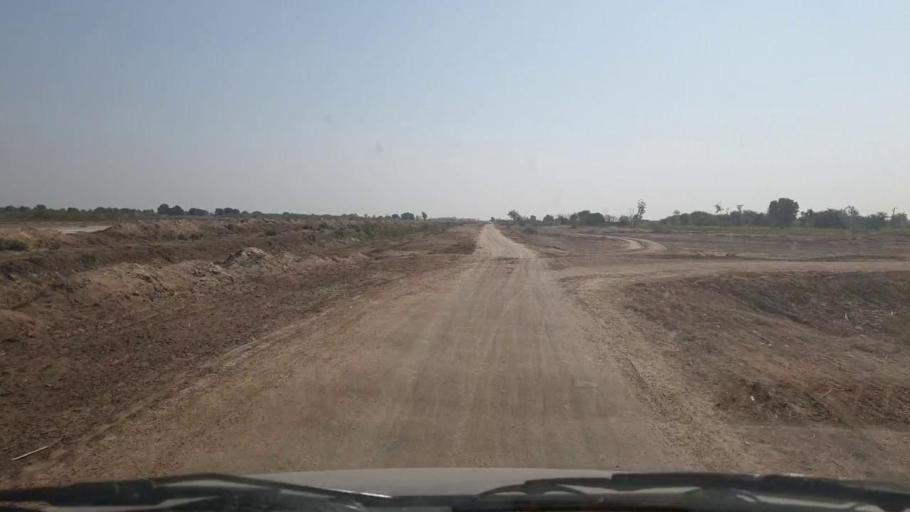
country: PK
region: Sindh
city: Samaro
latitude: 25.2543
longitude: 69.3258
